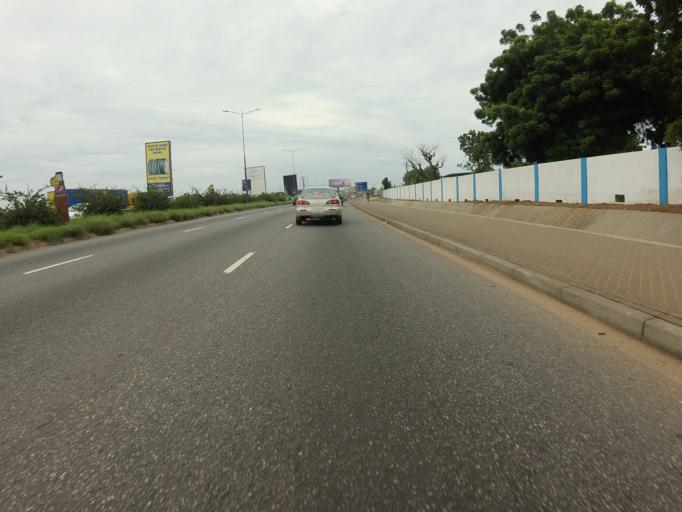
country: GH
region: Greater Accra
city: Accra
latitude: 5.5927
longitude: -0.2201
